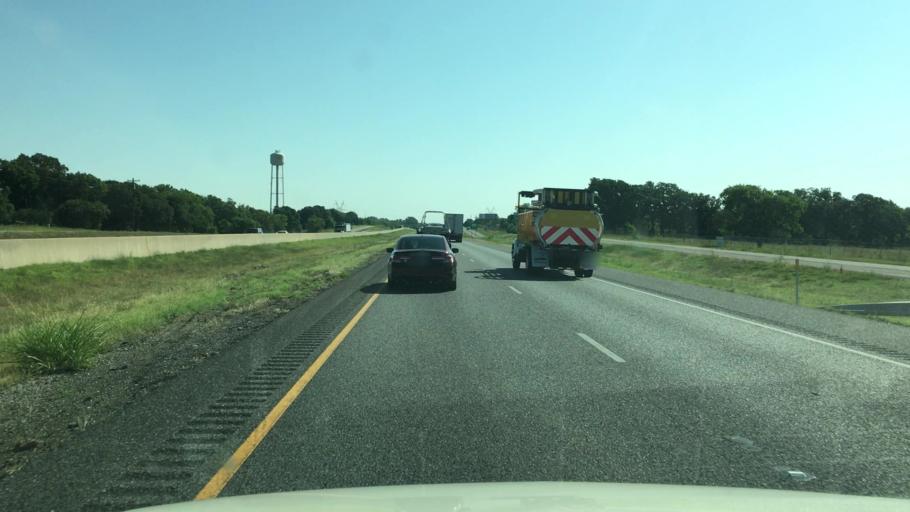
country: US
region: Texas
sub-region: Rockwall County
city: Royse City
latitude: 32.9895
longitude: -96.2554
